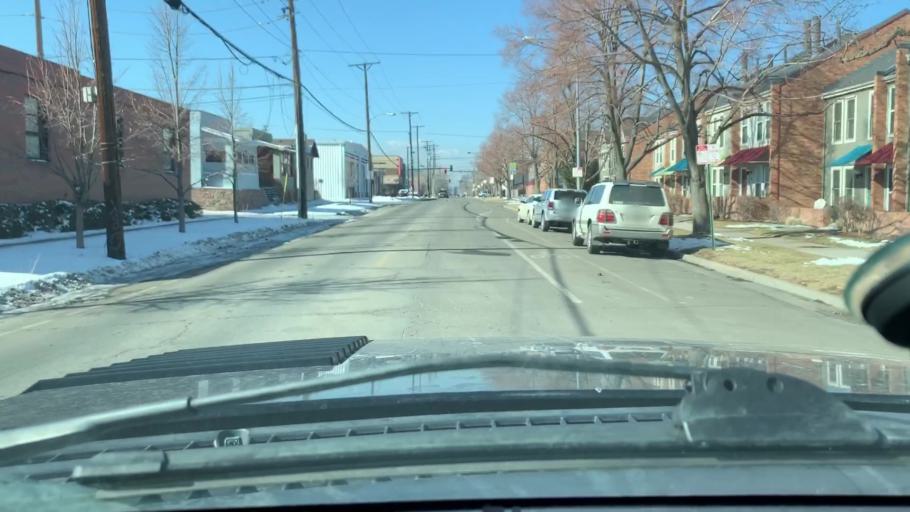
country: US
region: Colorado
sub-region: Denver County
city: Denver
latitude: 39.7337
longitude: -104.9967
